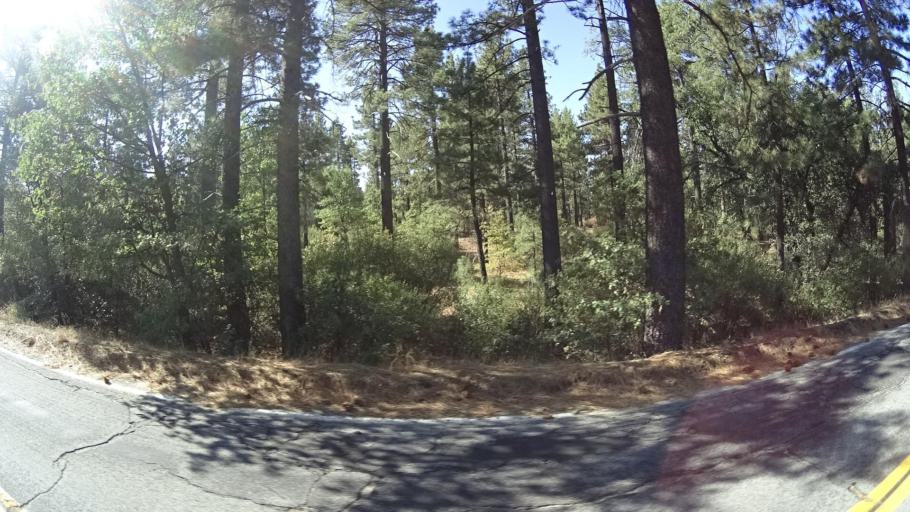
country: US
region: California
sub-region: San Diego County
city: Pine Valley
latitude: 32.8895
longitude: -116.4412
